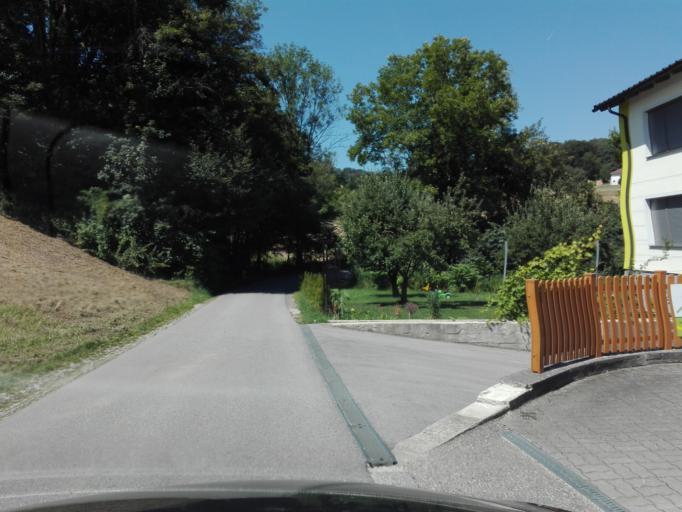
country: AT
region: Upper Austria
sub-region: Politischer Bezirk Urfahr-Umgebung
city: Steyregg
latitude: 48.2971
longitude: 14.3888
